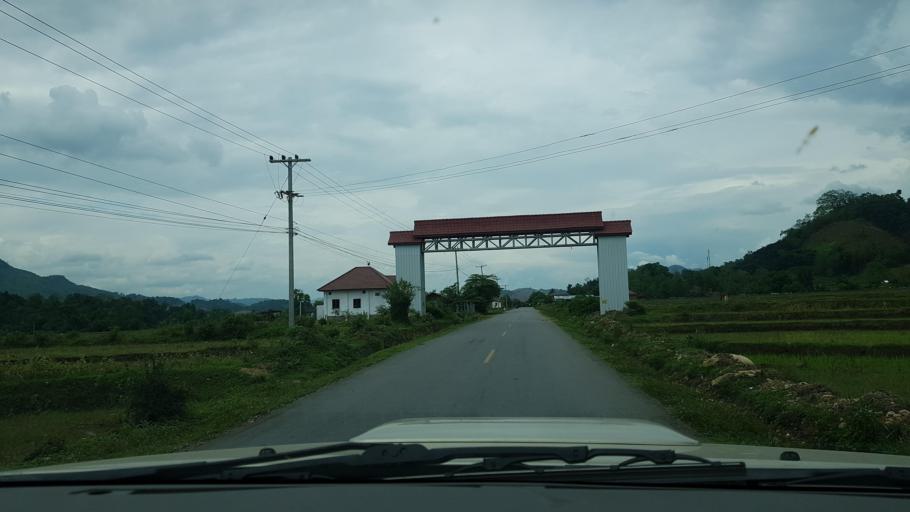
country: LA
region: Loungnamtha
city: Muang Nale
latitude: 20.3352
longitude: 101.6724
